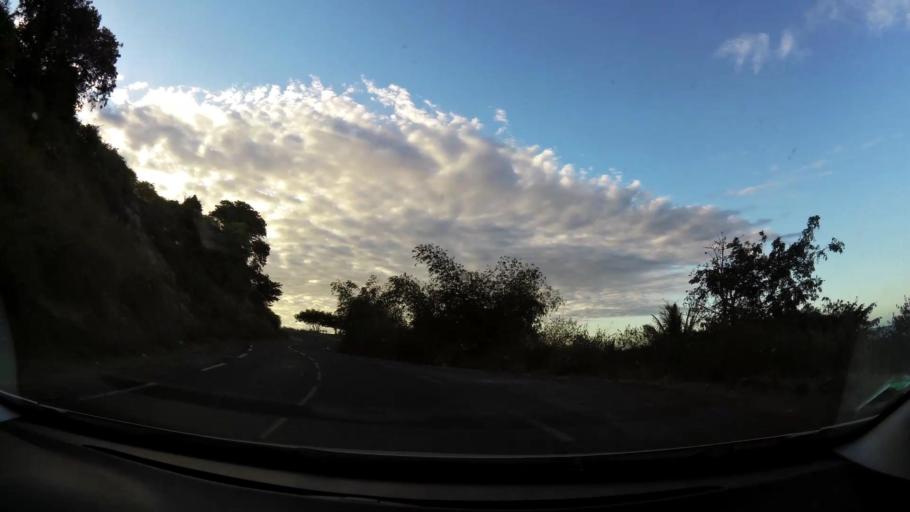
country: YT
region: Koungou
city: Koungou
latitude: -12.7315
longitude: 45.1983
